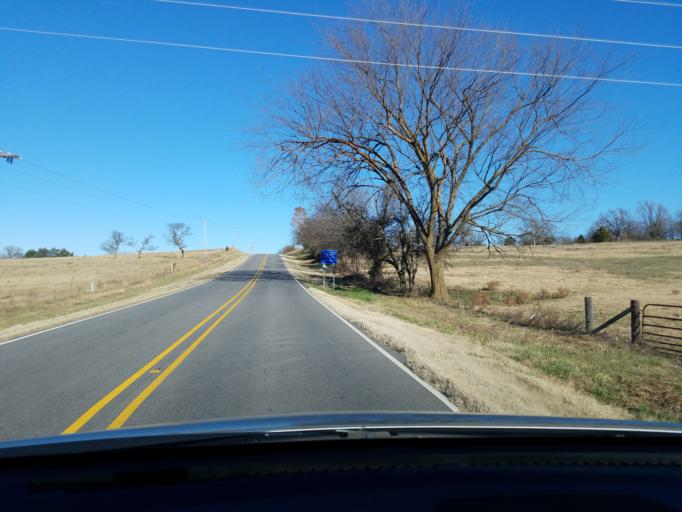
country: US
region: Arkansas
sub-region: Carroll County
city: Berryville
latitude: 36.3943
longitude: -93.5479
